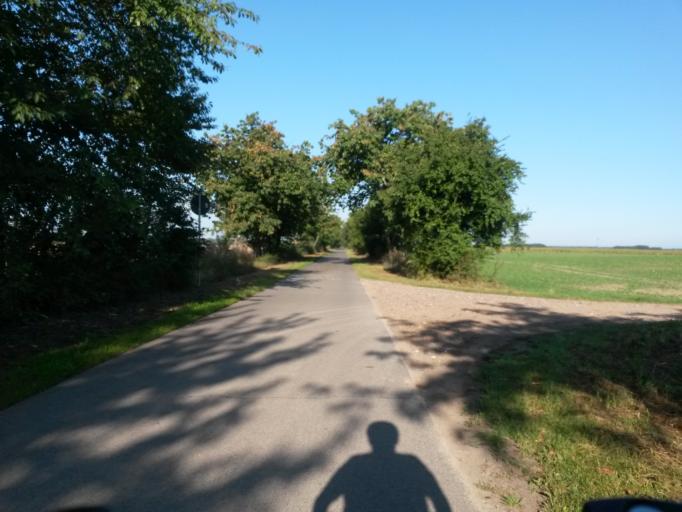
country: DE
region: Brandenburg
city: Templin
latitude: 53.1272
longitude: 13.4762
